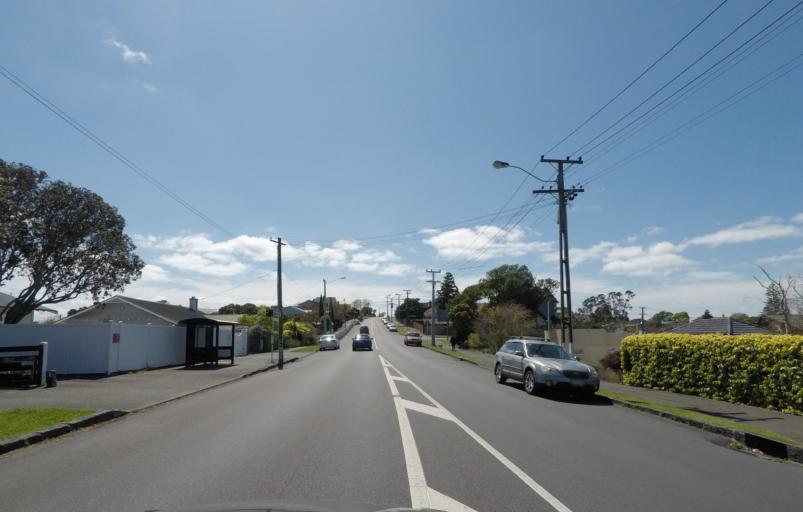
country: NZ
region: Auckland
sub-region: Auckland
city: Auckland
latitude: -36.8861
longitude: 174.8093
